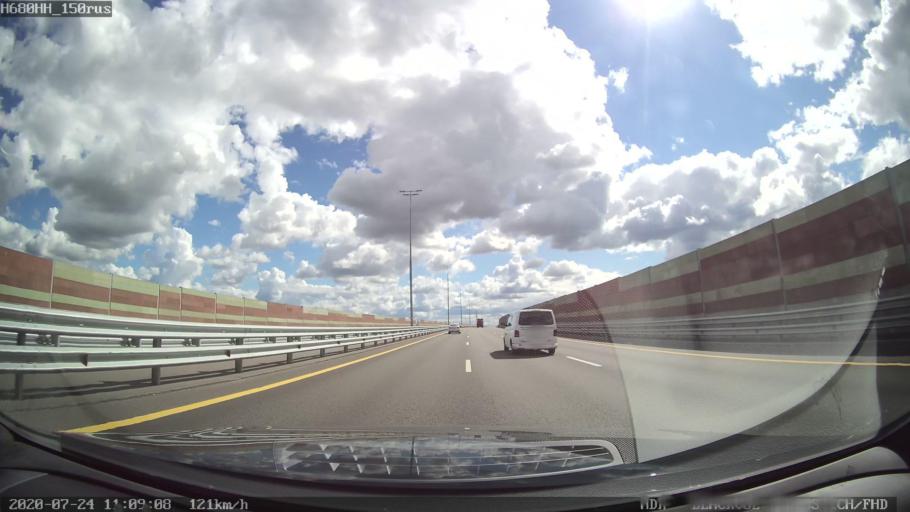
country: RU
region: St.-Petersburg
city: Tyarlevo
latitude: 59.7507
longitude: 30.4646
